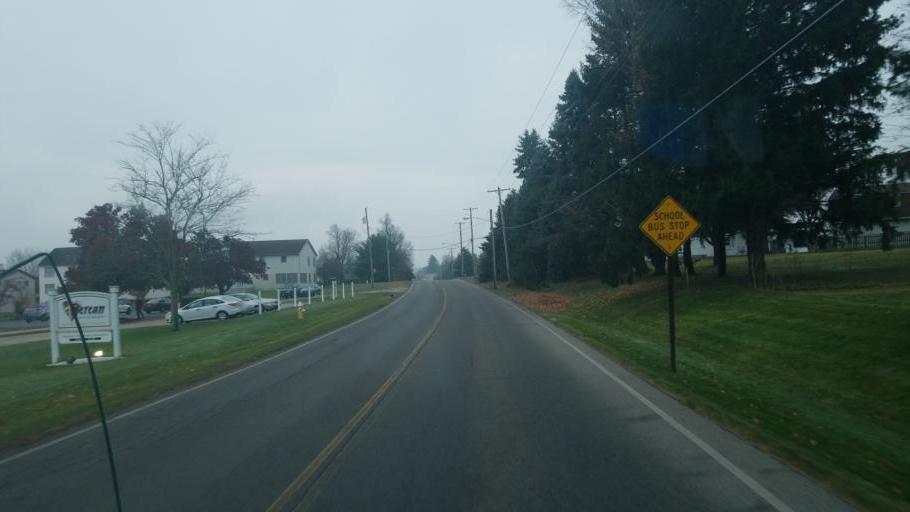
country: US
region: Ohio
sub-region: Richland County
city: Lexington
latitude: 40.7002
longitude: -82.5364
